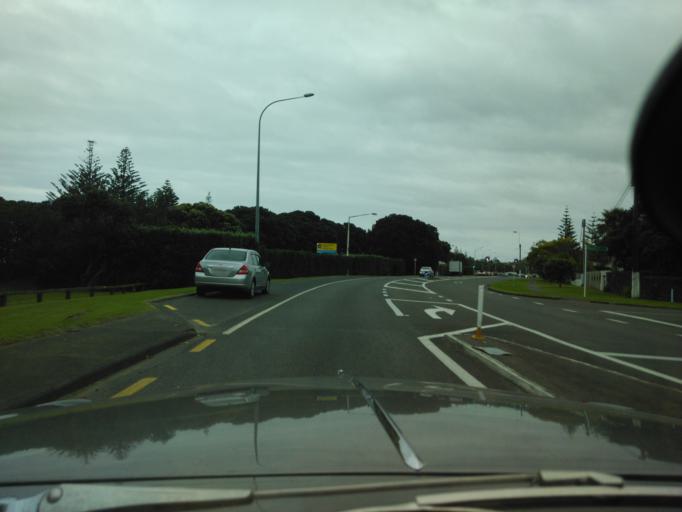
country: NZ
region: Auckland
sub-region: Auckland
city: Rothesay Bay
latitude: -36.5943
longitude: 174.6994
